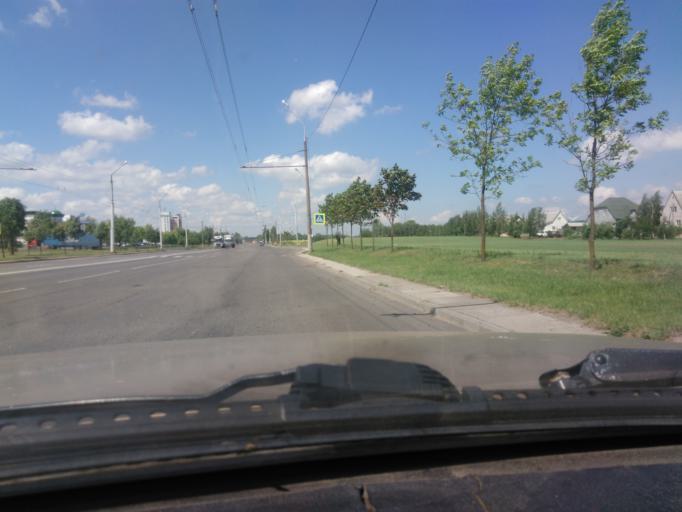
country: BY
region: Mogilev
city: Palykavichy Pyershyya
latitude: 53.9640
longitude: 30.3545
